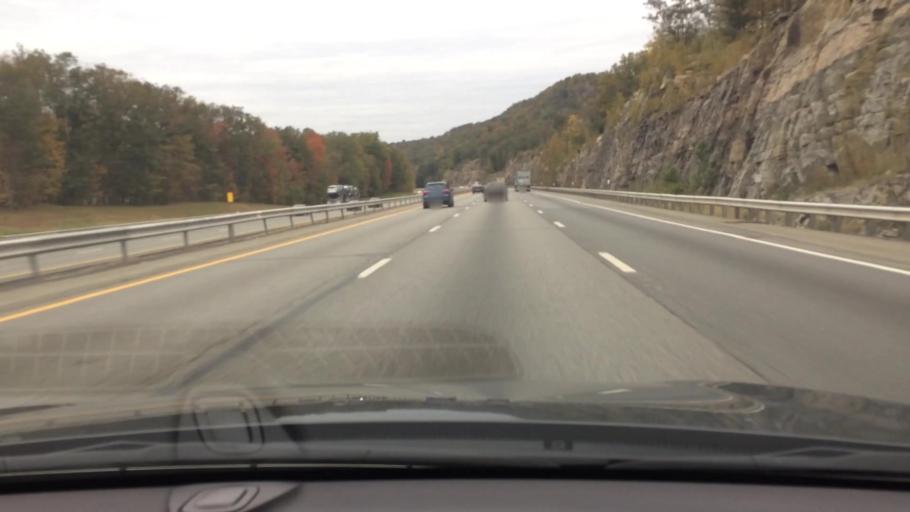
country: US
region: New York
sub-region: Rockland County
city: Sloatsburg
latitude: 41.1798
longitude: -74.1830
